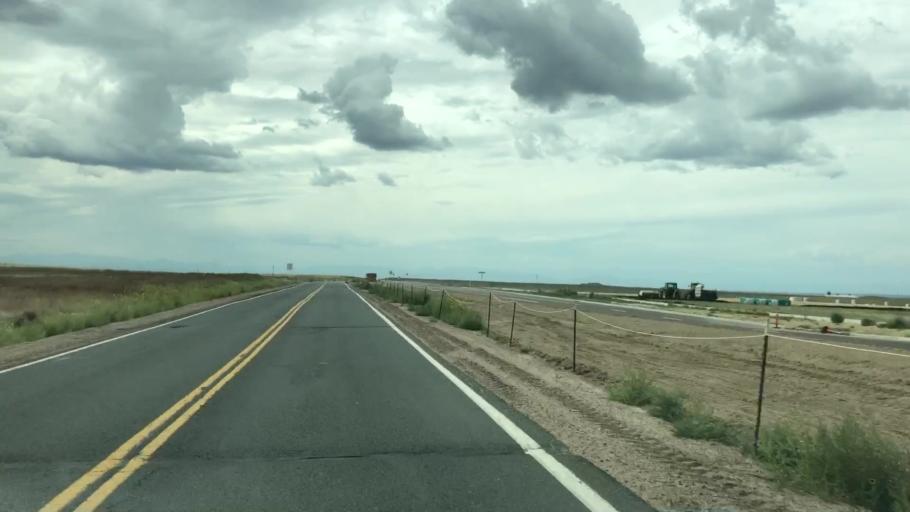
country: US
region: Colorado
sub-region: Adams County
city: Aurora
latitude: 39.7981
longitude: -104.6761
